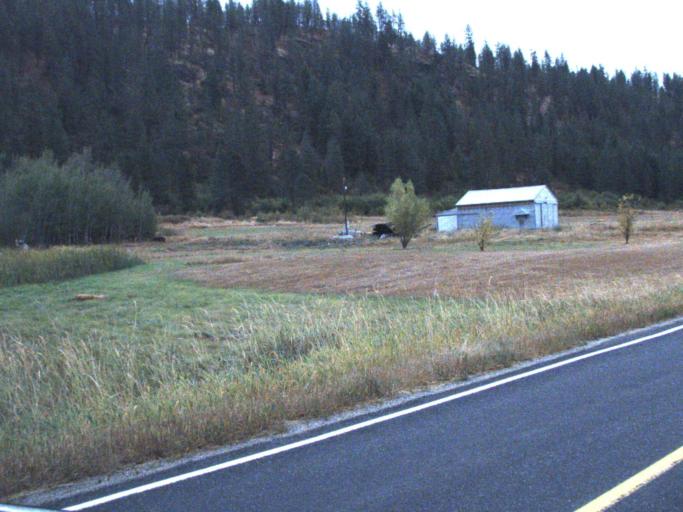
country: US
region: Washington
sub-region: Stevens County
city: Chewelah
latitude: 48.1881
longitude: -117.7326
